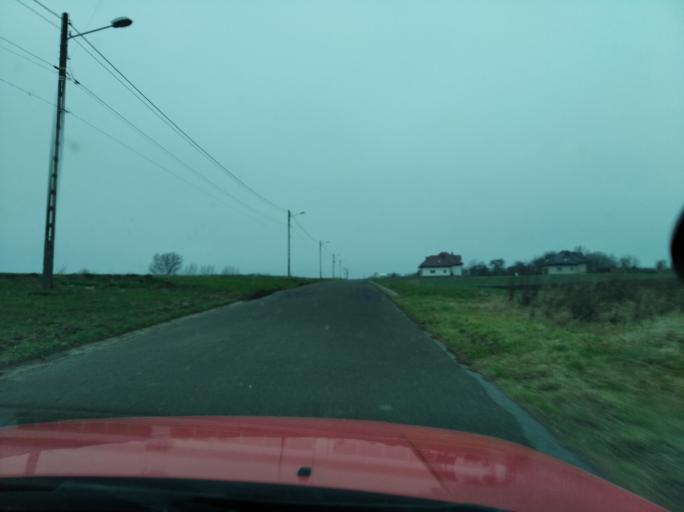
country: PL
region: Subcarpathian Voivodeship
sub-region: Powiat jaroslawski
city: Wierzbna
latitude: 50.0170
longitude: 22.6038
